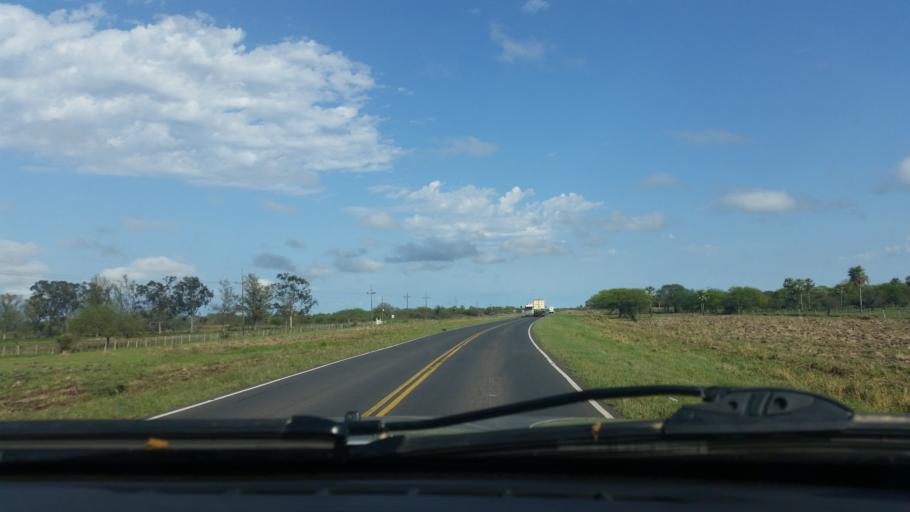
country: PY
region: Presidente Hayes
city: Benjamin Aceval
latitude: -24.9197
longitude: -57.6029
